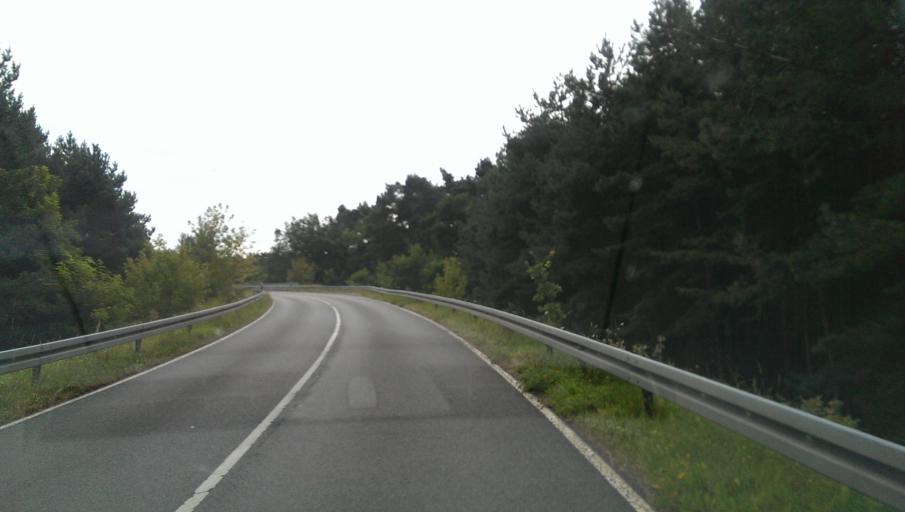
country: DE
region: Brandenburg
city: Trebbin
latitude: 52.1950
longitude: 13.2222
